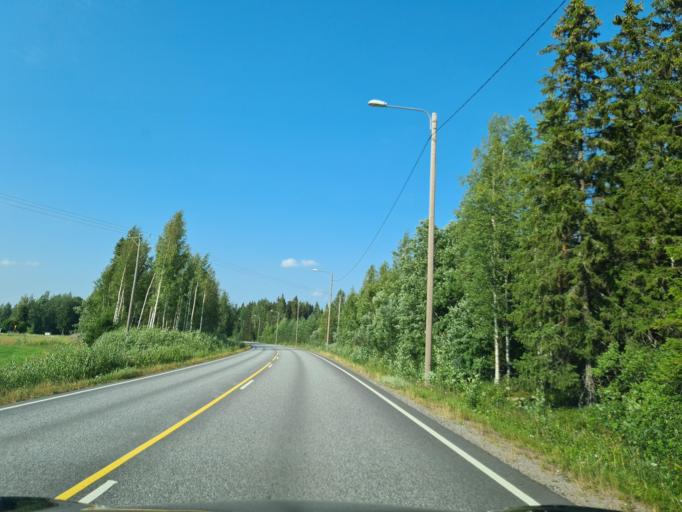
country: FI
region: Satakunta
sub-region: Pohjois-Satakunta
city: Karvia
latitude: 62.0836
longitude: 22.5253
